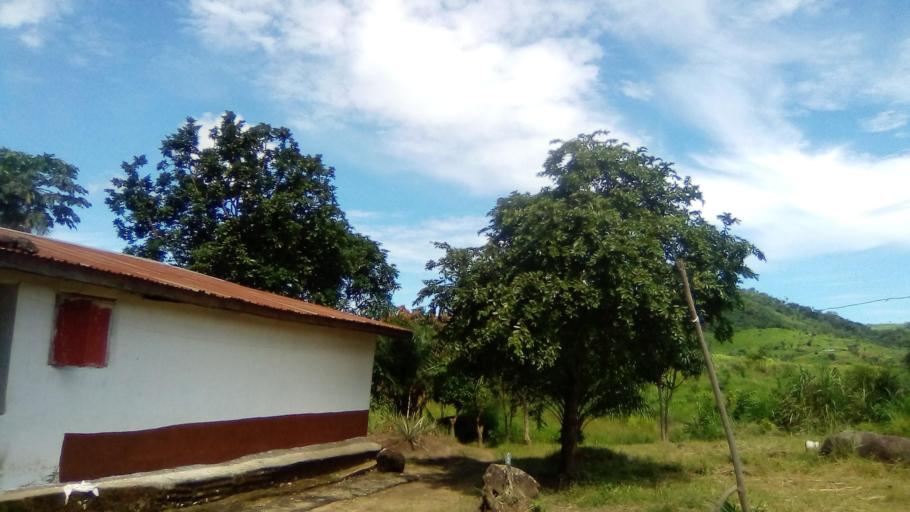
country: SL
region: Eastern Province
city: Simbakoro
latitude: 8.6376
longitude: -10.9985
